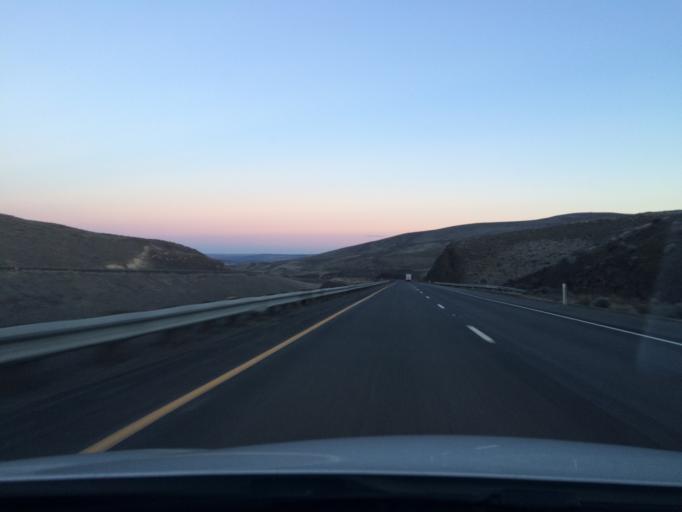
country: US
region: Washington
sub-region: Grant County
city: Mattawa
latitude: 46.9381
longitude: -120.0511
